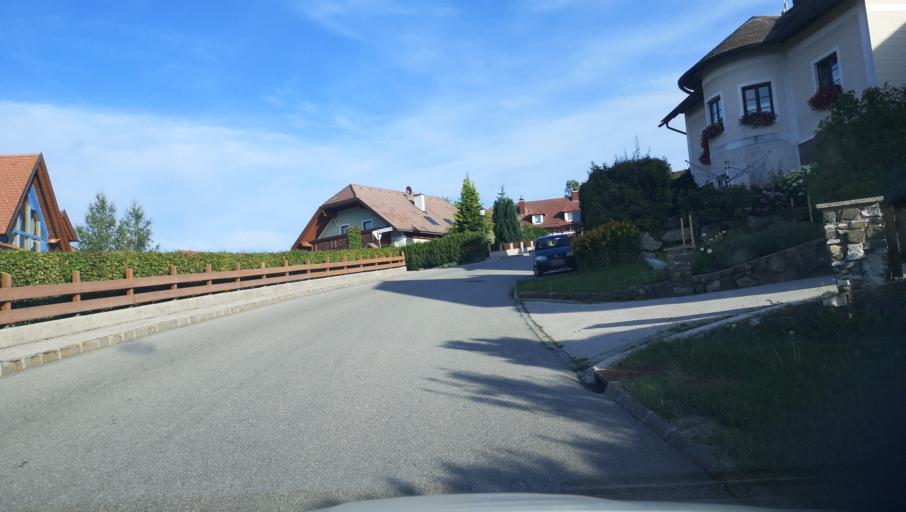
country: AT
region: Lower Austria
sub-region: Politischer Bezirk Amstetten
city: Neuhofen an der Ybbs
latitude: 47.9967
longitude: 14.8728
